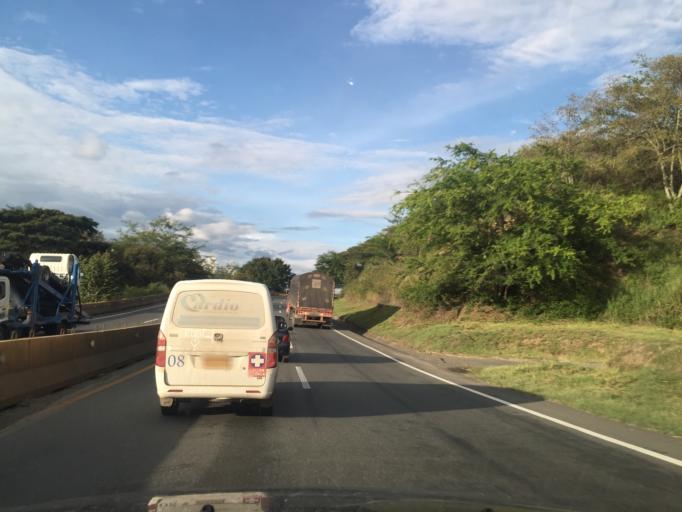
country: CO
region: Valle del Cauca
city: Bugalagrande
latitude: 4.2078
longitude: -76.1531
